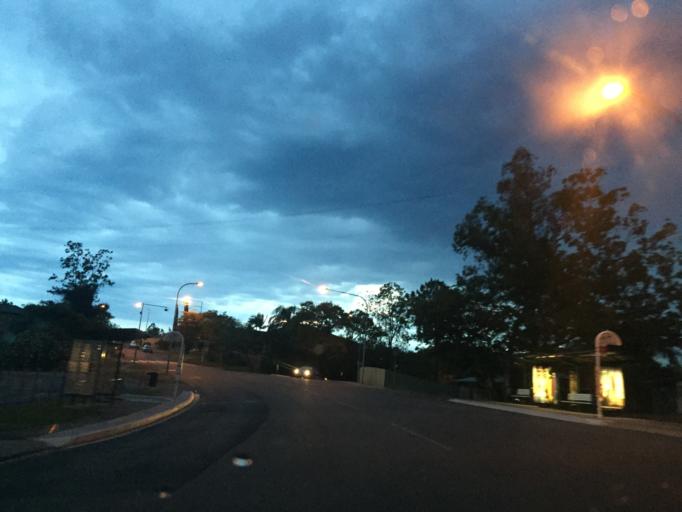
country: AU
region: Queensland
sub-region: Moreton Bay
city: Ferny Hills
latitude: -27.4420
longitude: 152.9391
